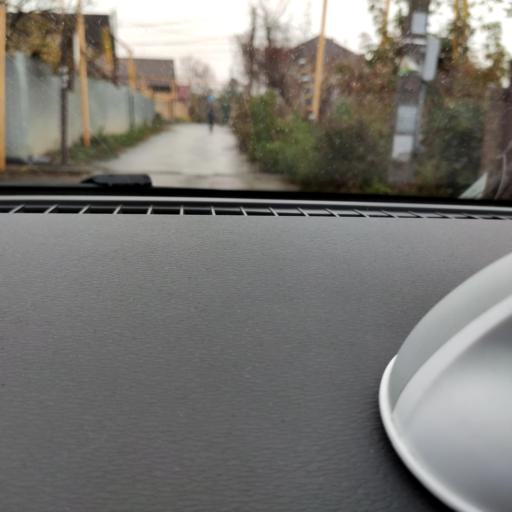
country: RU
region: Samara
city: Samara
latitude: 53.2724
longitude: 50.2095
